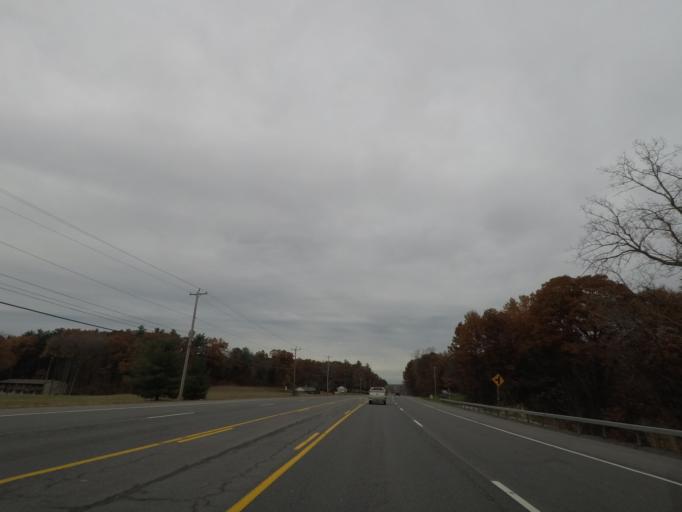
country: US
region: New York
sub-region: Saratoga County
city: Country Knolls
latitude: 42.8822
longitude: -73.7740
